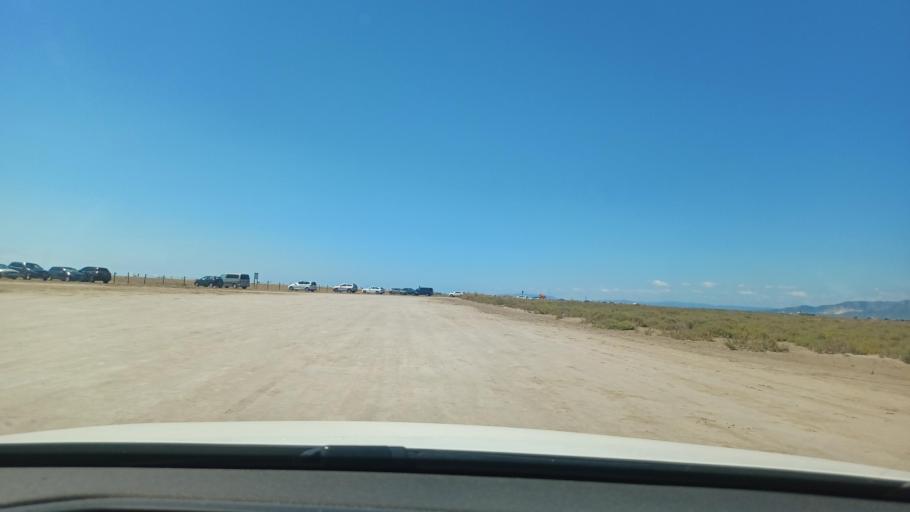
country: ES
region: Catalonia
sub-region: Provincia de Tarragona
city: Deltebre
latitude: 40.6534
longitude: 0.7811
